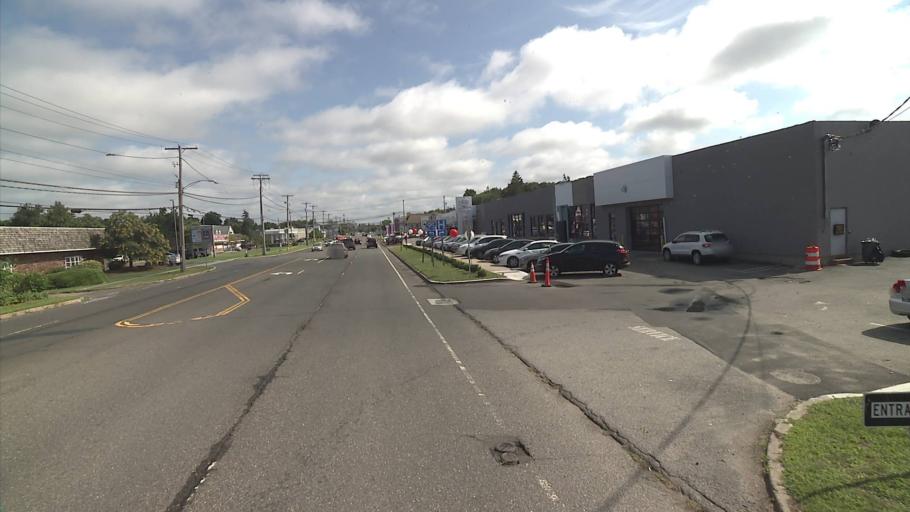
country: US
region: Connecticut
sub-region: New Haven County
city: City of Milford (balance)
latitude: 41.2205
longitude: -73.0739
